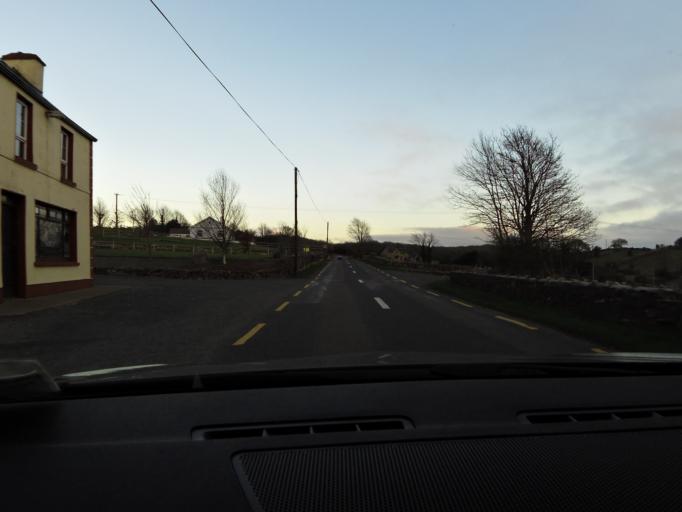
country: IE
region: Connaught
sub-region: Sligo
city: Ballymote
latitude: 53.9756
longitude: -8.4512
